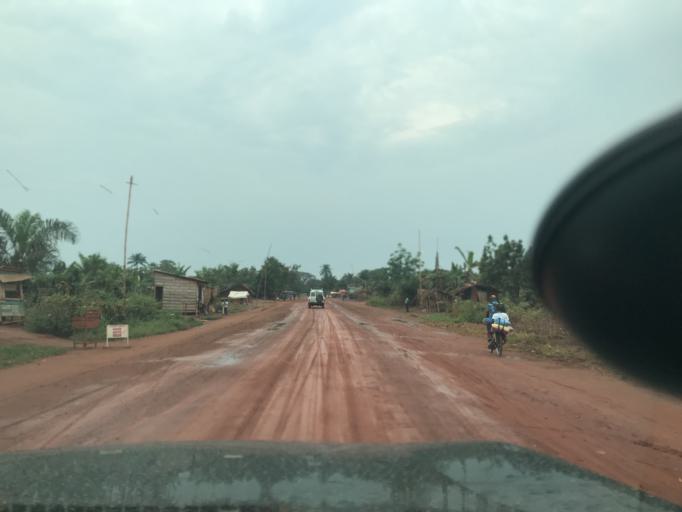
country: CD
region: Equateur
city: Gemena
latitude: 3.2317
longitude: 19.7803
